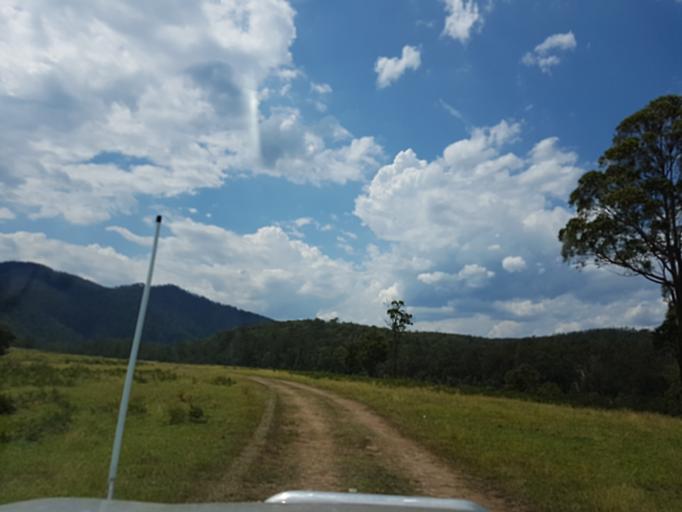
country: AU
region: Victoria
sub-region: East Gippsland
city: Lakes Entrance
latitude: -37.4027
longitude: 148.3334
